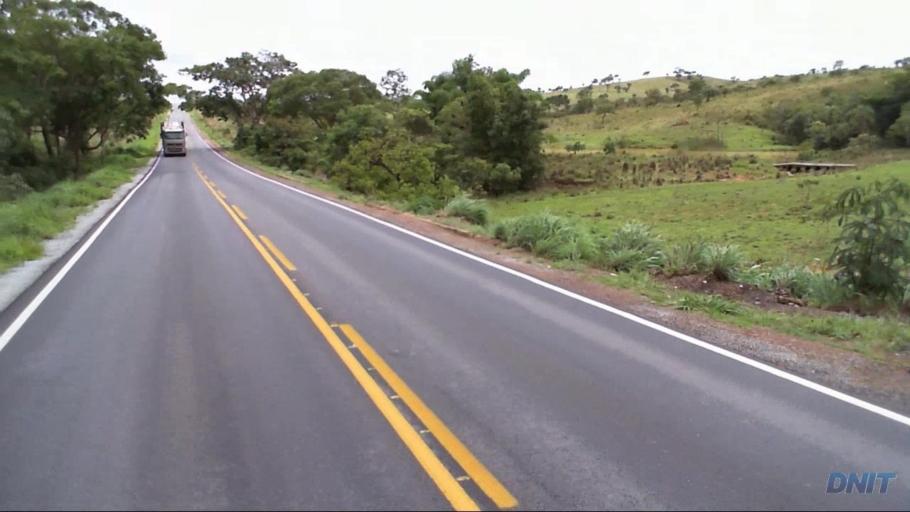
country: BR
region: Goias
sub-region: Padre Bernardo
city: Padre Bernardo
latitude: -15.4742
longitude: -48.2312
